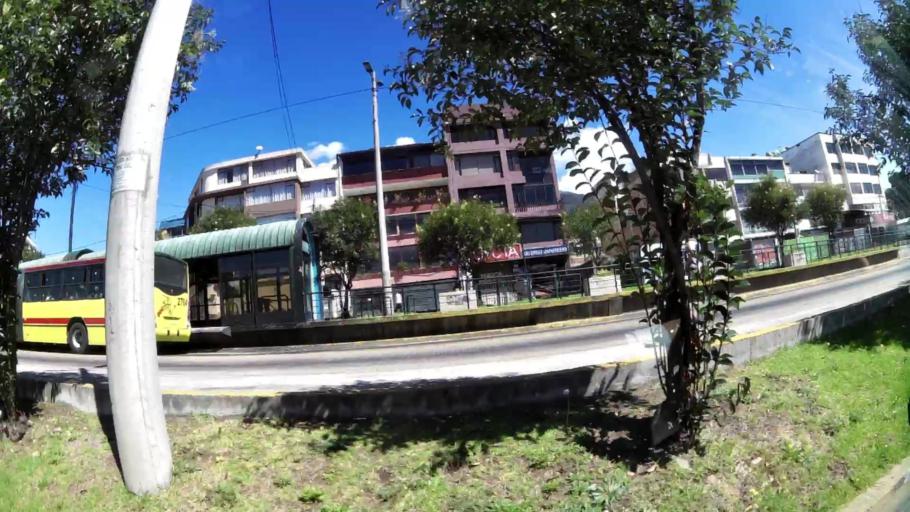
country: EC
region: Pichincha
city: Quito
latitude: -0.1786
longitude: -78.4941
